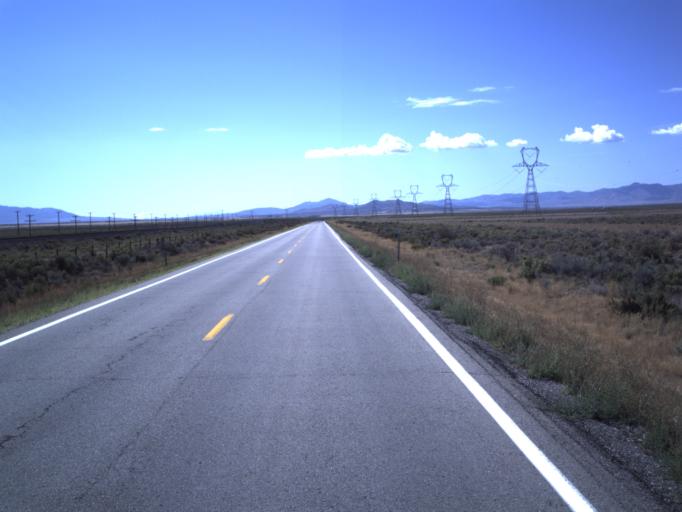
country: US
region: Utah
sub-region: Tooele County
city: Tooele
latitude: 40.2852
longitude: -112.3996
